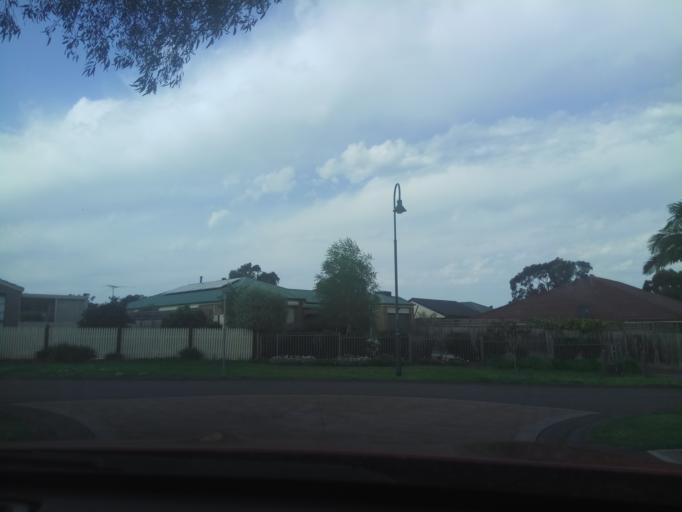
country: AU
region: Victoria
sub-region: Casey
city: Lynbrook
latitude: -38.0486
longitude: 145.2522
